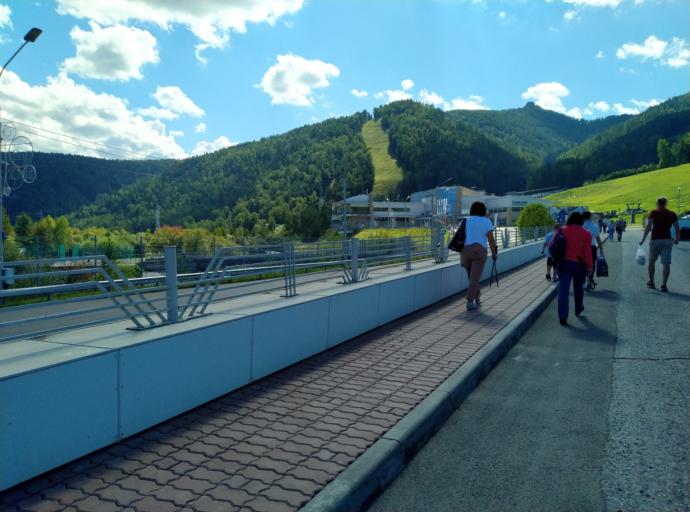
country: RU
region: Krasnoyarskiy
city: Krasnoyarsk
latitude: 55.9633
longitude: 92.7938
